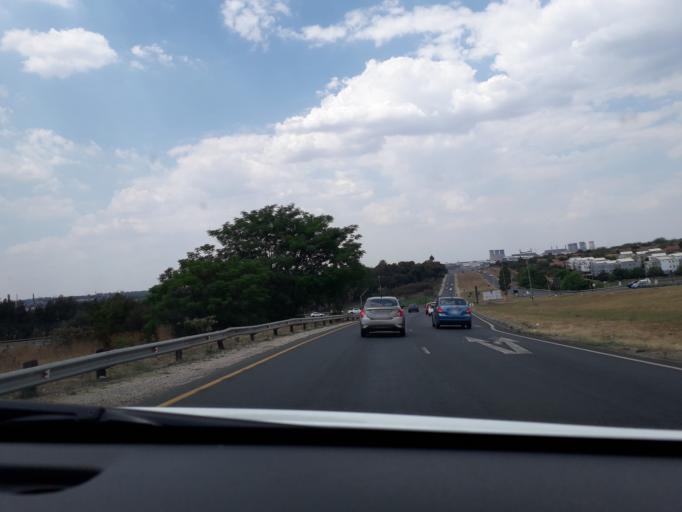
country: ZA
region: Gauteng
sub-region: City of Johannesburg Metropolitan Municipality
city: Modderfontein
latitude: -26.1098
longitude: 28.1480
